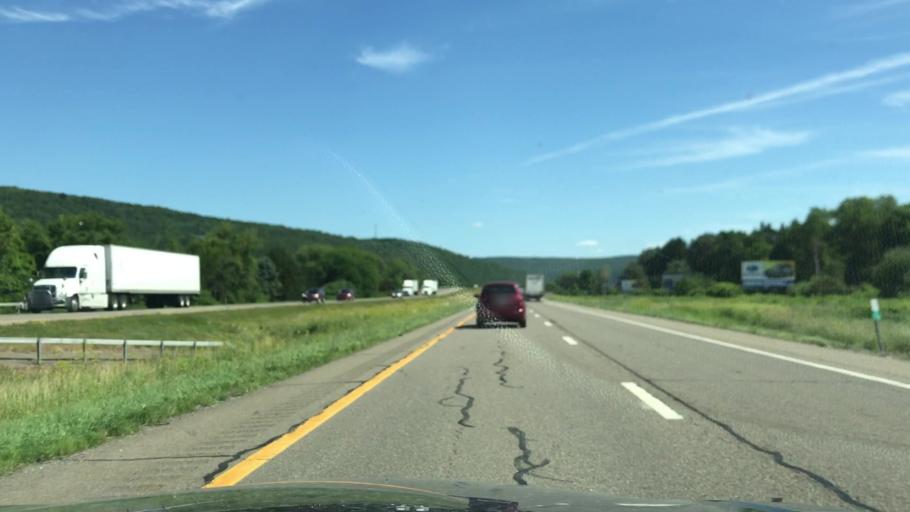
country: US
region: New York
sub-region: Steuben County
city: Gang Mills
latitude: 42.2111
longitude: -77.1733
